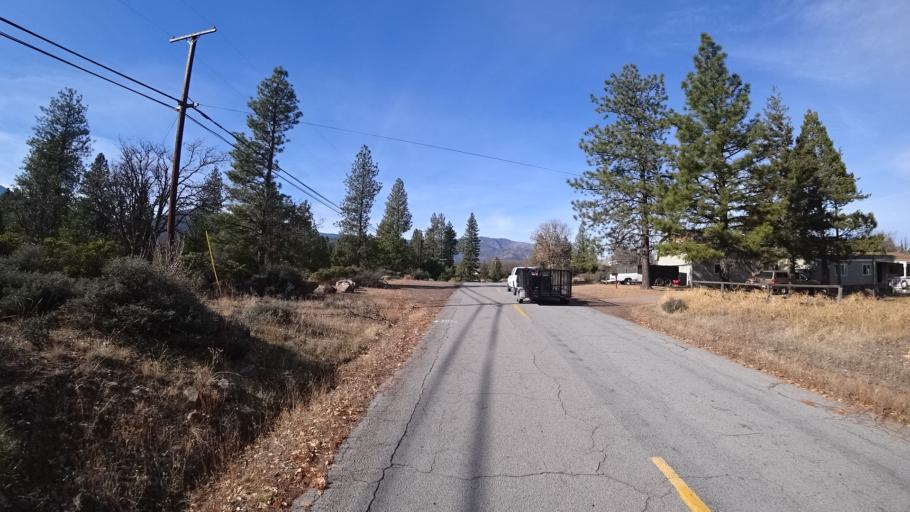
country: US
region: California
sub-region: Siskiyou County
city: Weed
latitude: 41.4298
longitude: -122.4217
